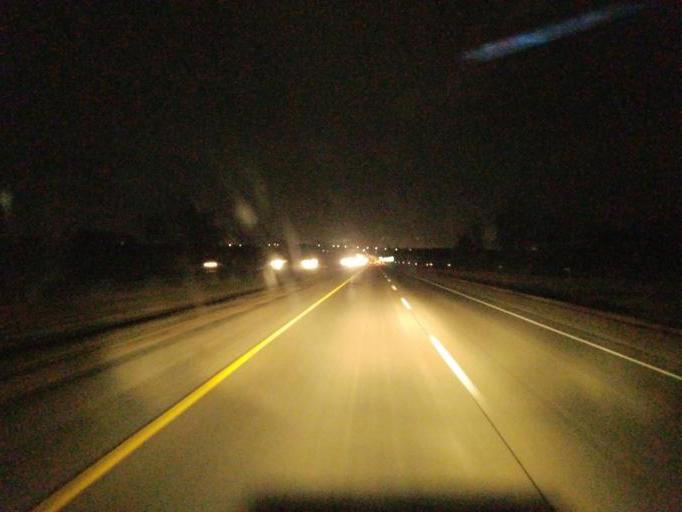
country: US
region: Iowa
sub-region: Dallas County
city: Waukee
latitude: 41.5631
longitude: -93.8784
